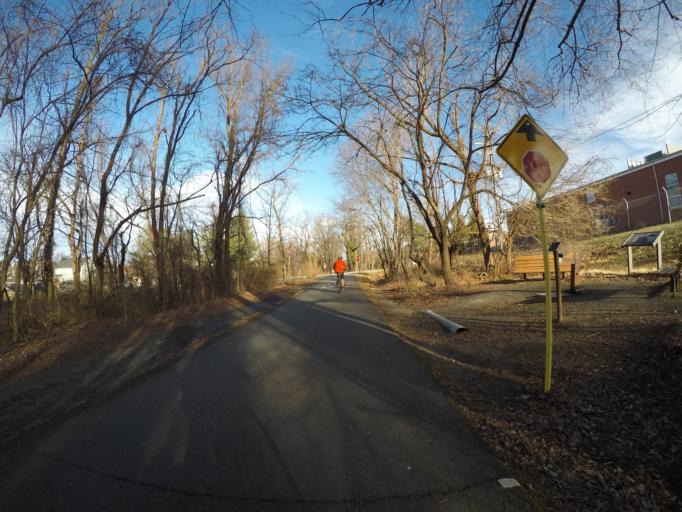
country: US
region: Virginia
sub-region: Loudoun County
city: Leesburg
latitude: 39.1123
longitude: -77.5793
